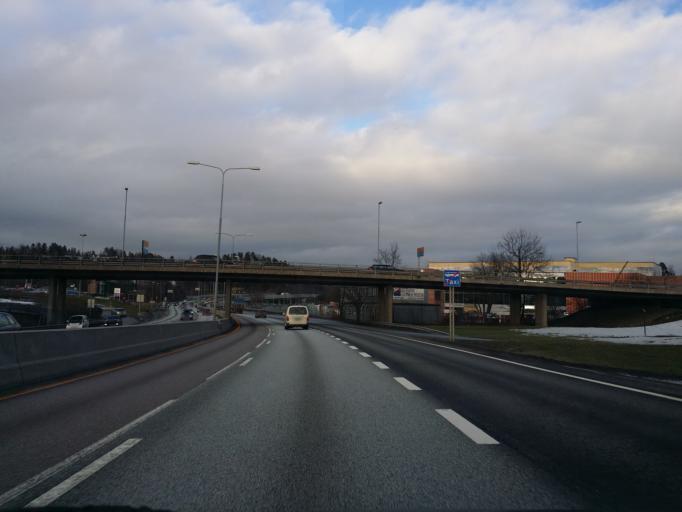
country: NO
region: Akershus
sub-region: Asker
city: Billingstad
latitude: 59.8745
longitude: 10.5014
